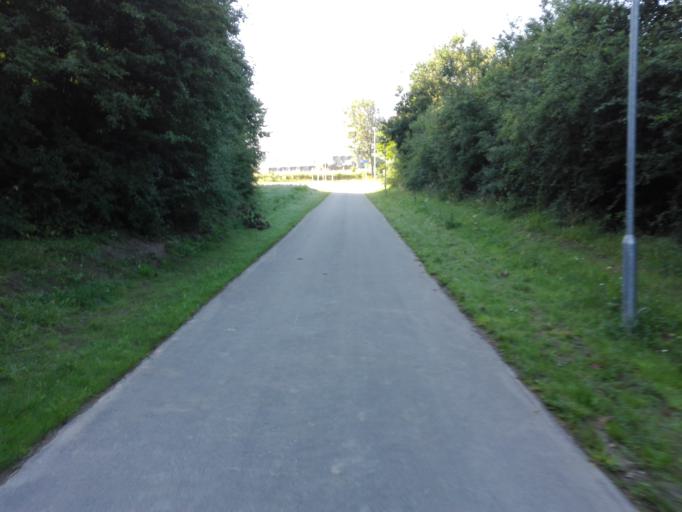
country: DK
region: Central Jutland
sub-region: Arhus Kommune
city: Tranbjerg
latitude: 56.0842
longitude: 10.1431
